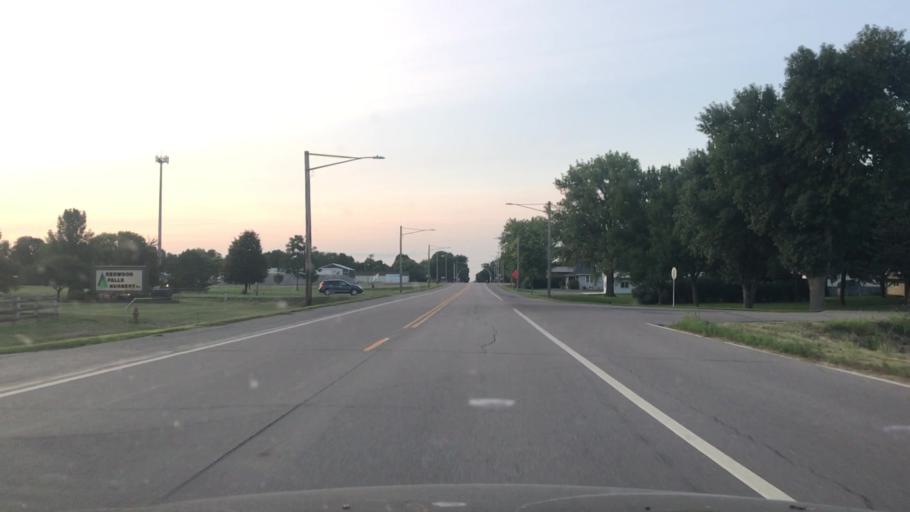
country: US
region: Minnesota
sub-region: Redwood County
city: Redwood Falls
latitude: 44.5285
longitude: -95.1195
